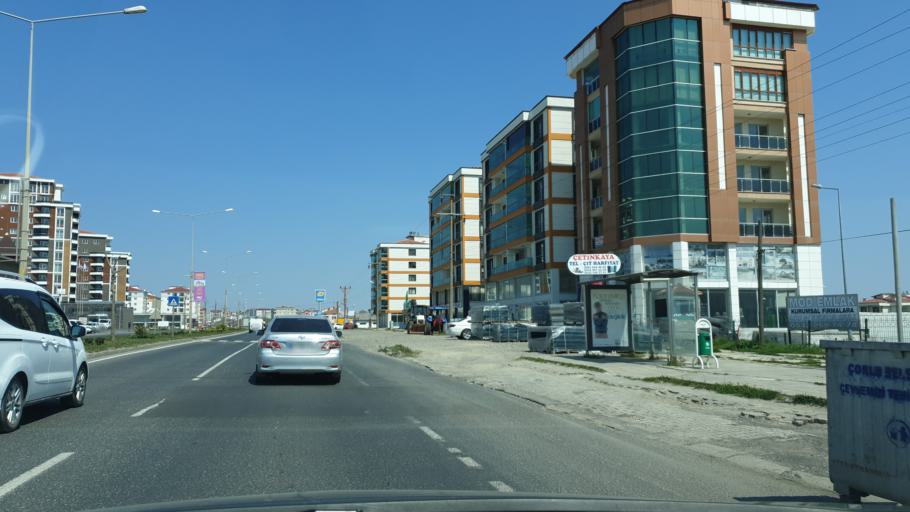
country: TR
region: Tekirdag
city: Corlu
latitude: 41.1533
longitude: 27.7798
